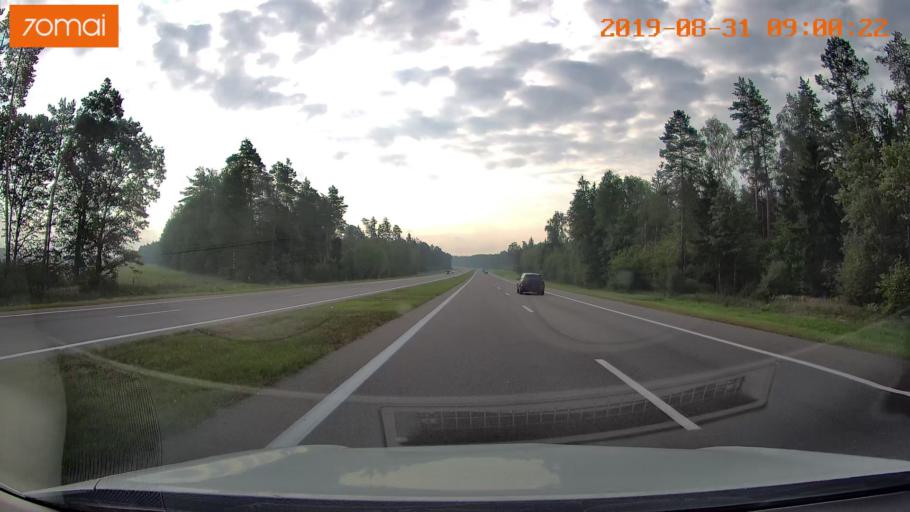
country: BY
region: Minsk
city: Chervyen'
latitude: 53.7587
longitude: 28.2346
